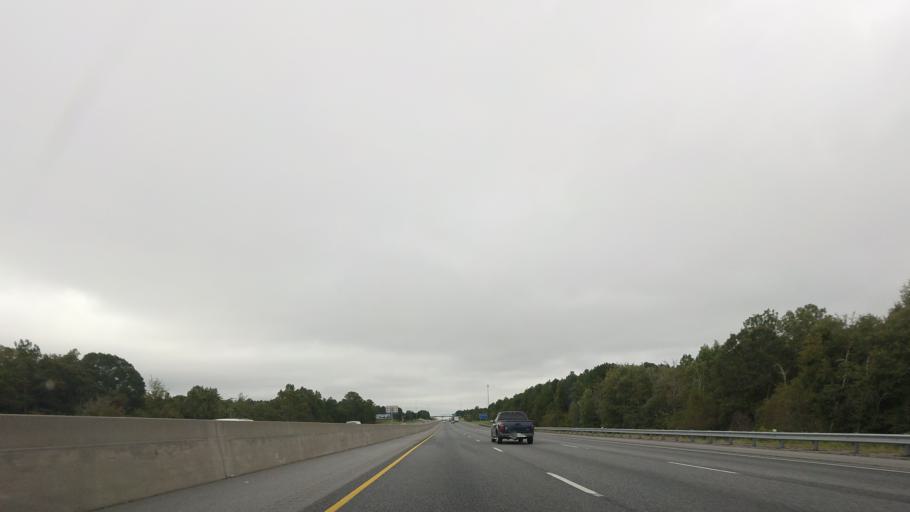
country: US
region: Georgia
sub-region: Tift County
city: Tifton
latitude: 31.5575
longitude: -83.5383
